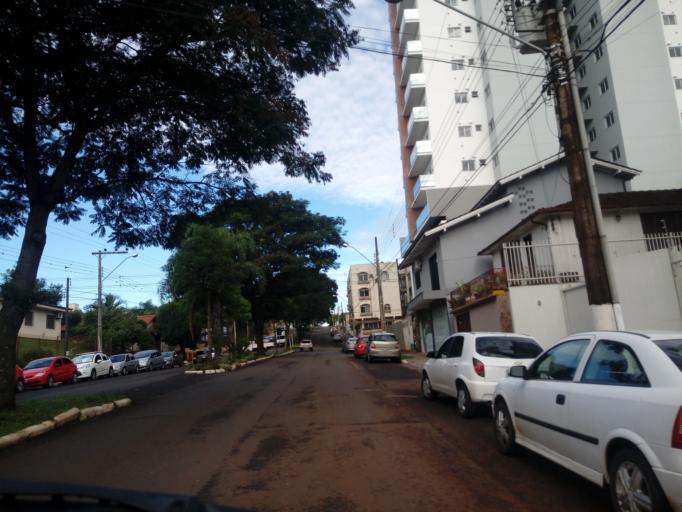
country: BR
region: Santa Catarina
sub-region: Chapeco
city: Chapeco
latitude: -27.1059
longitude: -52.6196
